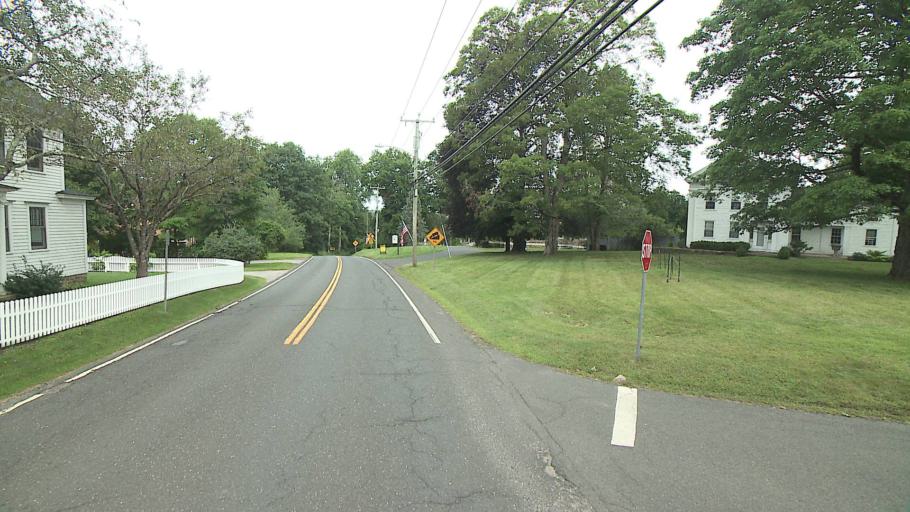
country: US
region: Connecticut
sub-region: Litchfield County
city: New Preston
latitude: 41.6311
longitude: -73.3125
